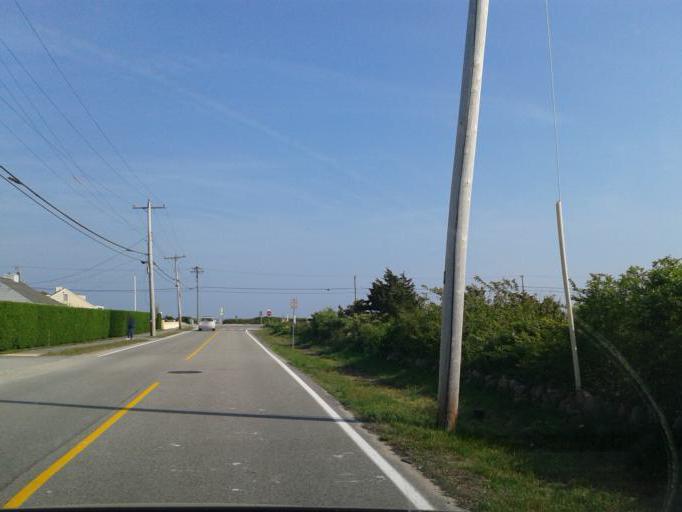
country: US
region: Massachusetts
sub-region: Barnstable County
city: Falmouth
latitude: 41.5426
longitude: -70.6241
